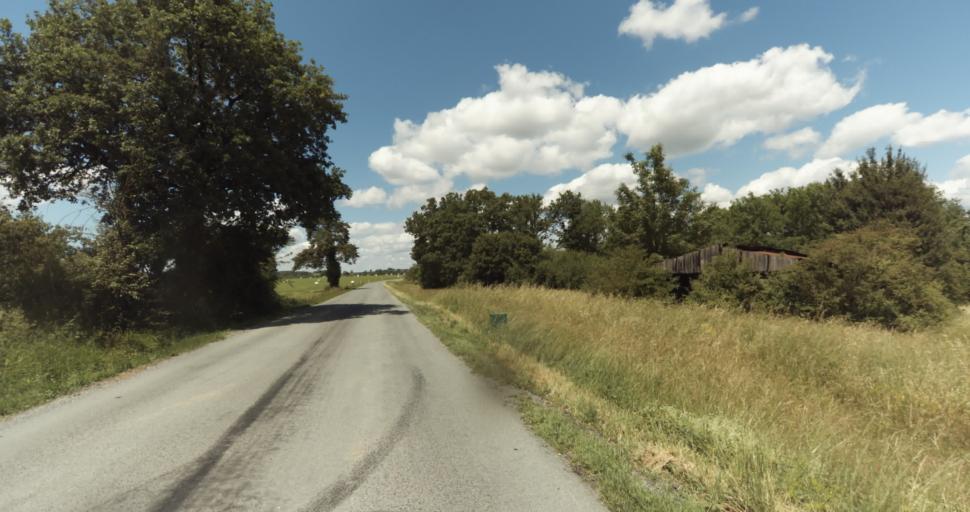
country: FR
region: Aquitaine
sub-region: Departement de la Dordogne
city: Beaumont-du-Perigord
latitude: 44.7099
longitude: 0.8115
